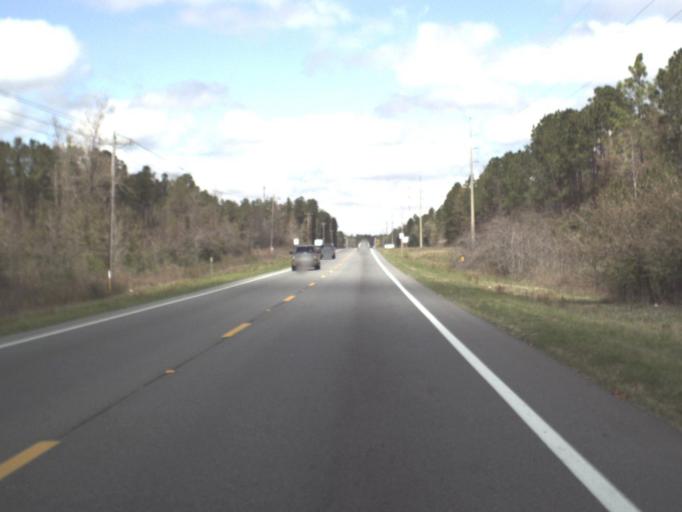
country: US
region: Florida
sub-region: Wakulla County
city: Crawfordville
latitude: 30.2560
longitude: -84.3622
